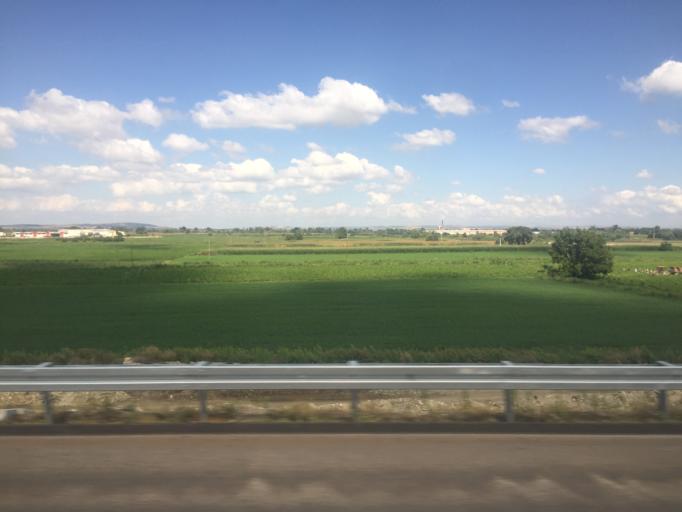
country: TR
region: Balikesir
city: Gobel
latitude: 40.0665
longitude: 28.2470
